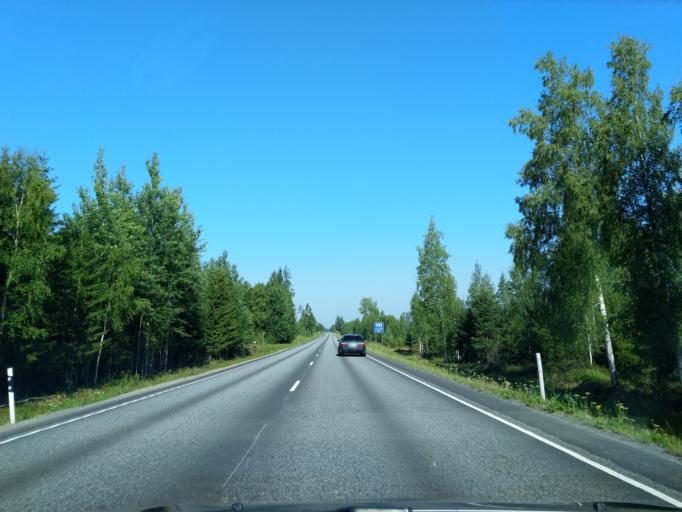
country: FI
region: Satakunta
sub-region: Pori
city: Huittinen
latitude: 61.1308
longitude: 22.7900
